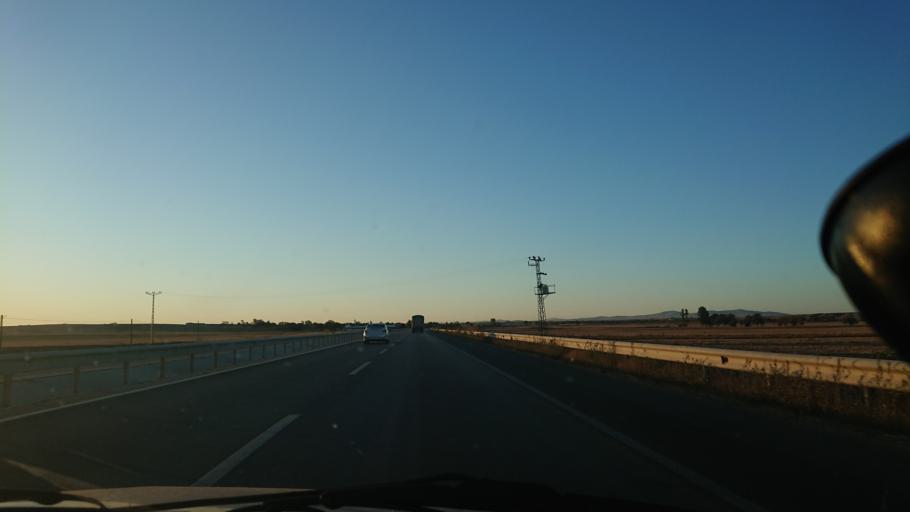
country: TR
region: Eskisehir
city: Mahmudiye
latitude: 39.5284
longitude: 30.9515
